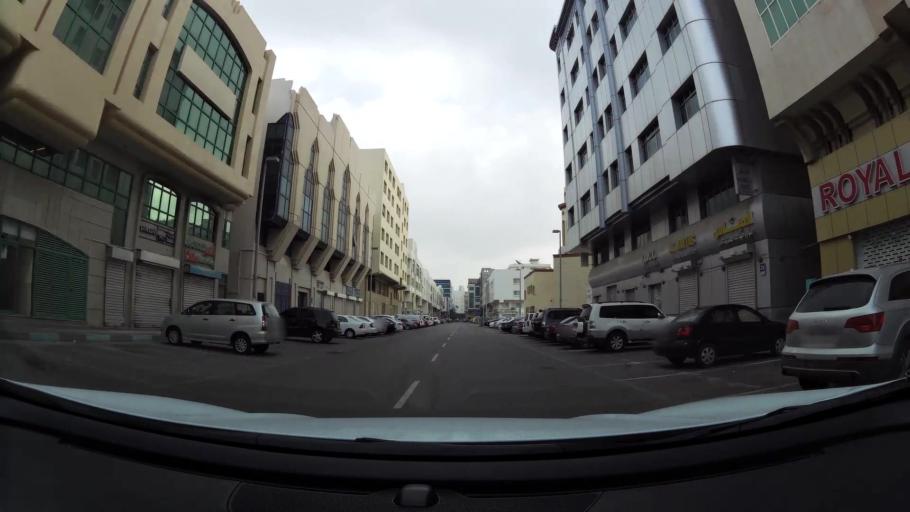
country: AE
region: Abu Dhabi
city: Abu Dhabi
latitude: 24.4747
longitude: 54.3782
